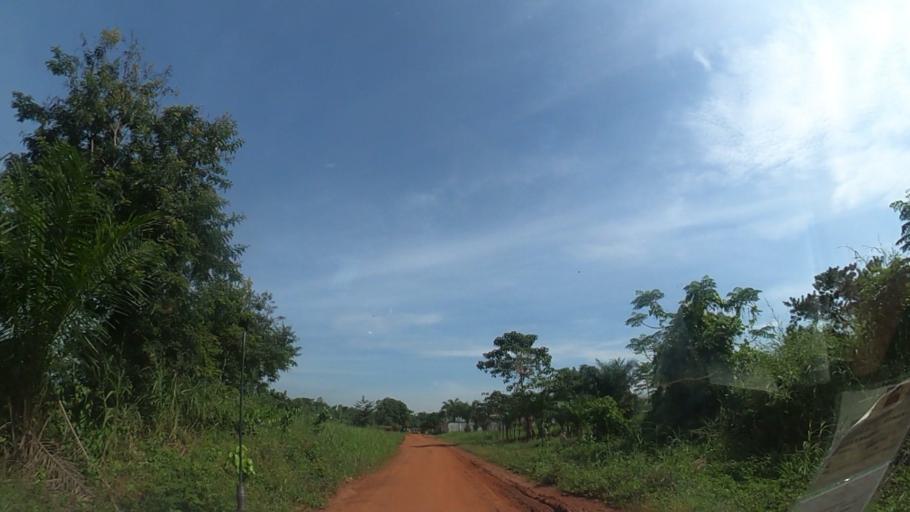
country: CF
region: Ombella-Mpoko
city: Bimbo
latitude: 4.3150
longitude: 18.4690
